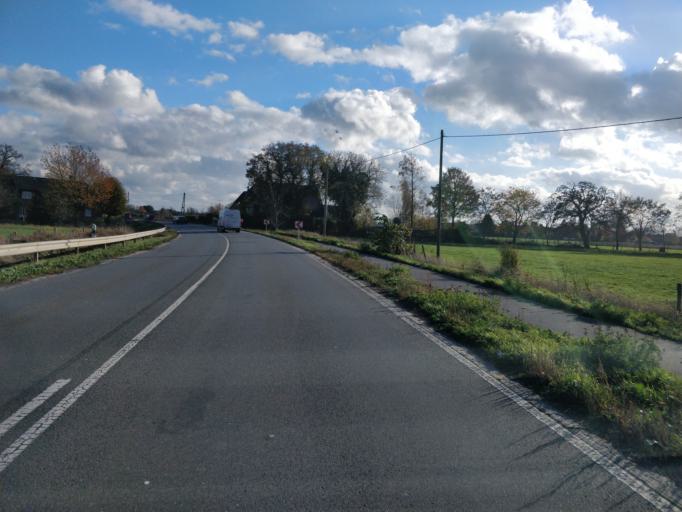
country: DE
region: North Rhine-Westphalia
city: Rees
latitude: 51.7760
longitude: 6.3803
